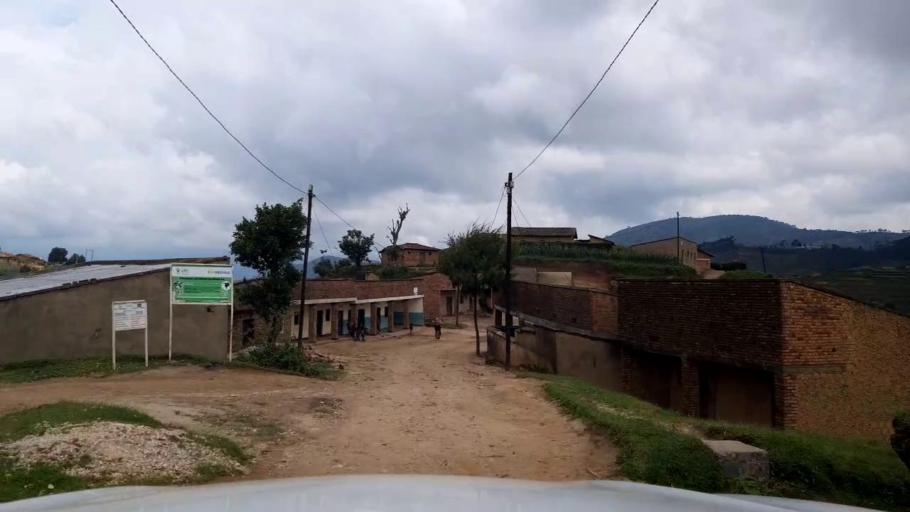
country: RW
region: Western Province
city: Kibuye
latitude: -1.9467
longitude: 29.4718
